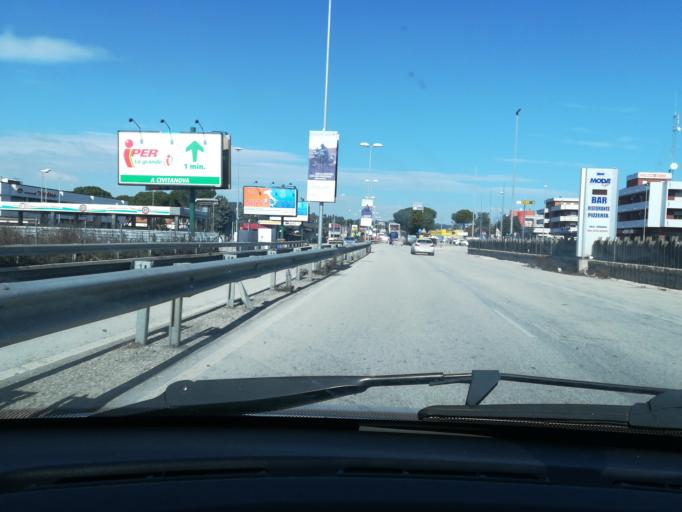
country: IT
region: The Marches
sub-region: Provincia di Macerata
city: Santa Maria Apparente
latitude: 43.2906
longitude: 13.7074
